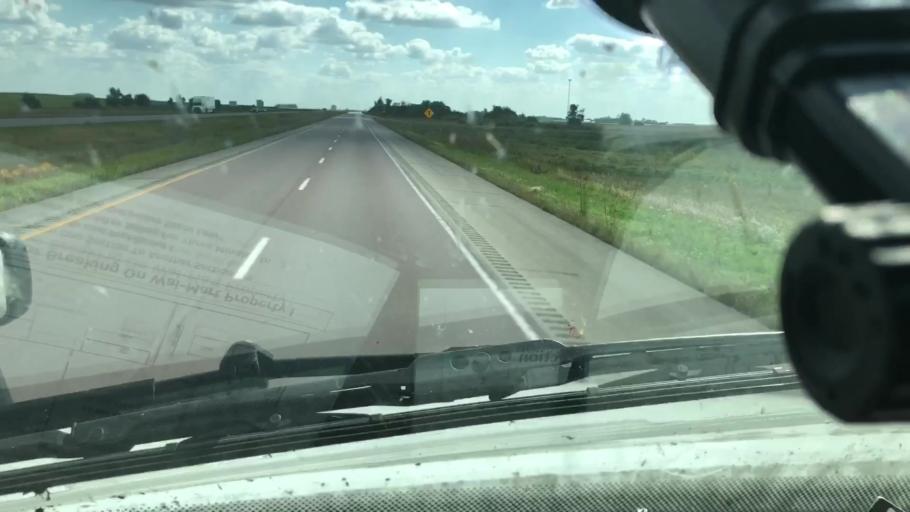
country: US
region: Iowa
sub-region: Worth County
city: Northwood
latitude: 43.3564
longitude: -93.3492
